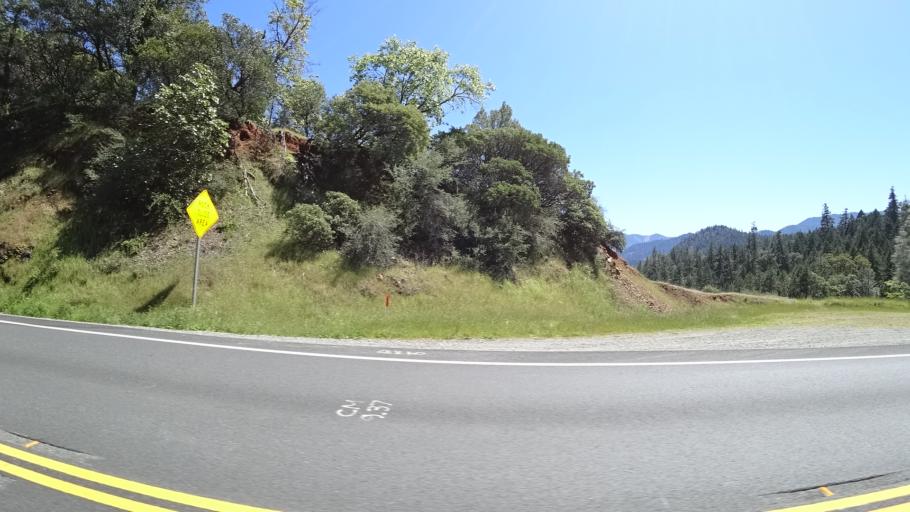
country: US
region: California
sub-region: Humboldt County
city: Willow Creek
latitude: 40.8358
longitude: -123.4873
